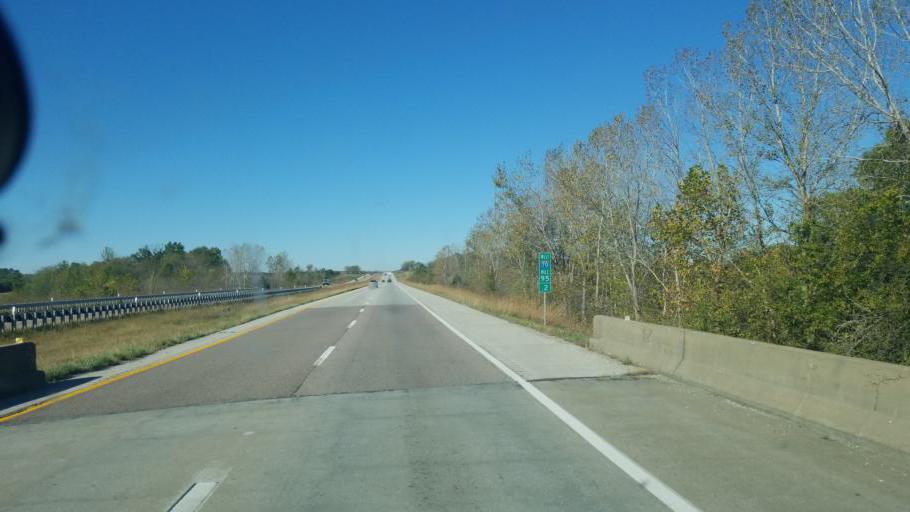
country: US
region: Missouri
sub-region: Cooper County
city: Boonville
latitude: 38.9349
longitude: -92.9009
